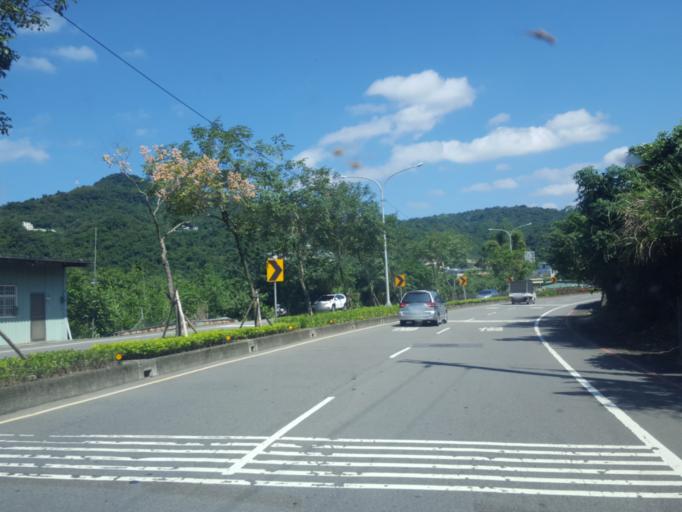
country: TW
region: Taipei
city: Taipei
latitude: 25.0074
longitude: 121.6322
